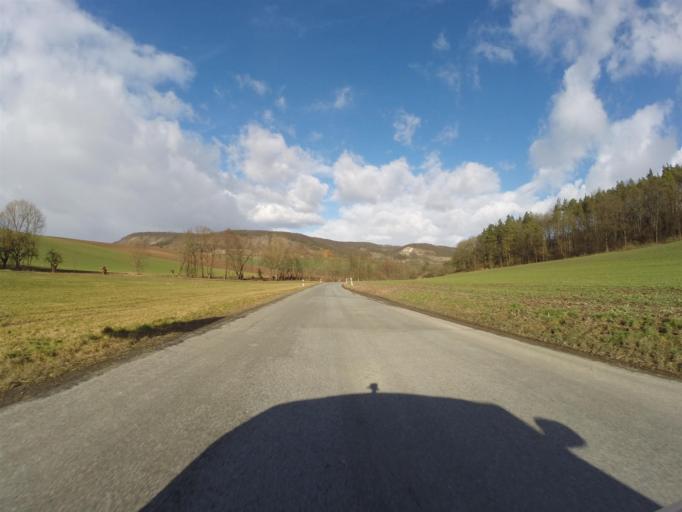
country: DE
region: Thuringia
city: Loberschutz
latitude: 50.9599
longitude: 11.6923
